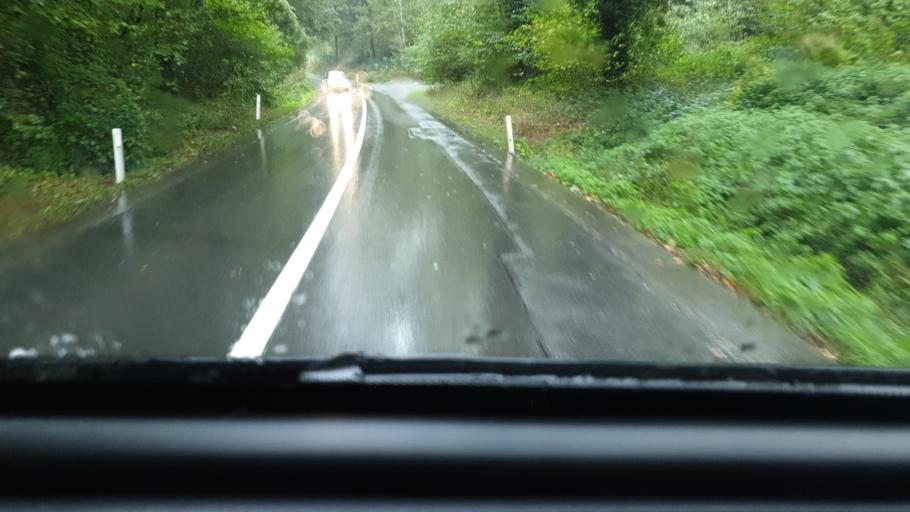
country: BE
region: Wallonia
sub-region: Province du Hainaut
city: Charleroi
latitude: 50.3670
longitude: 4.4776
